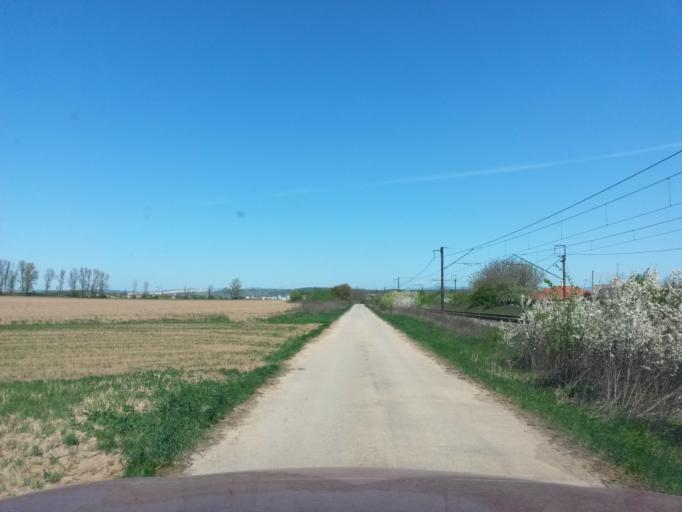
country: SK
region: Kosicky
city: Kosice
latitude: 48.6557
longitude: 21.2606
